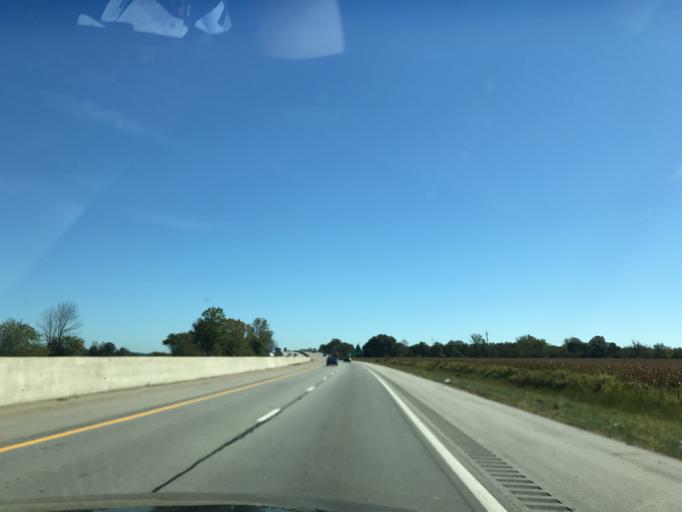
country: US
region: Ohio
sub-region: Licking County
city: Hebron
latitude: 39.9418
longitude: -82.5260
